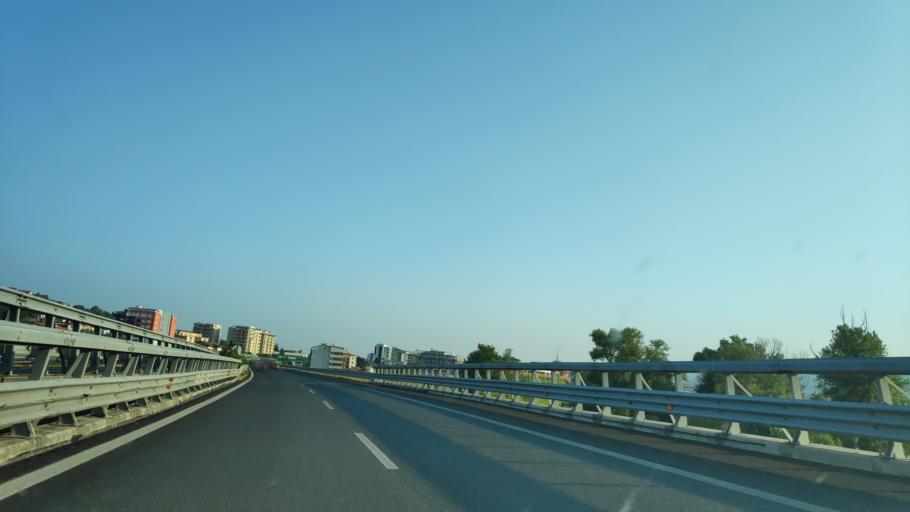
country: IT
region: Calabria
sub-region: Provincia di Cosenza
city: Cosenza
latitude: 39.3185
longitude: 16.2413
